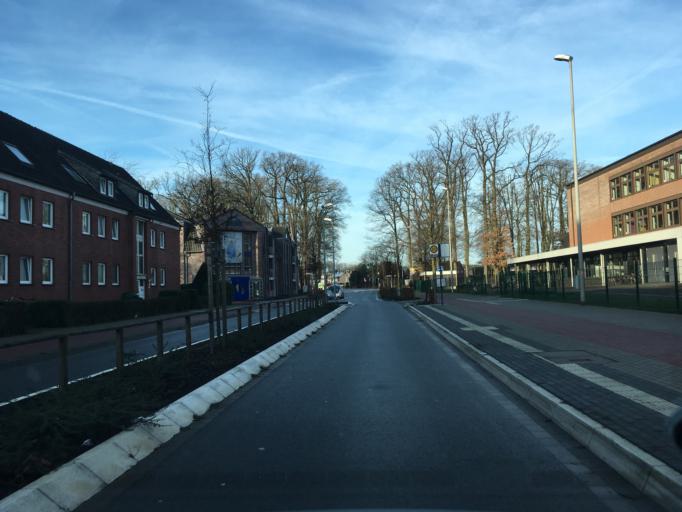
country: DE
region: North Rhine-Westphalia
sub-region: Regierungsbezirk Munster
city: Ahaus
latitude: 52.0844
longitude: 7.0094
